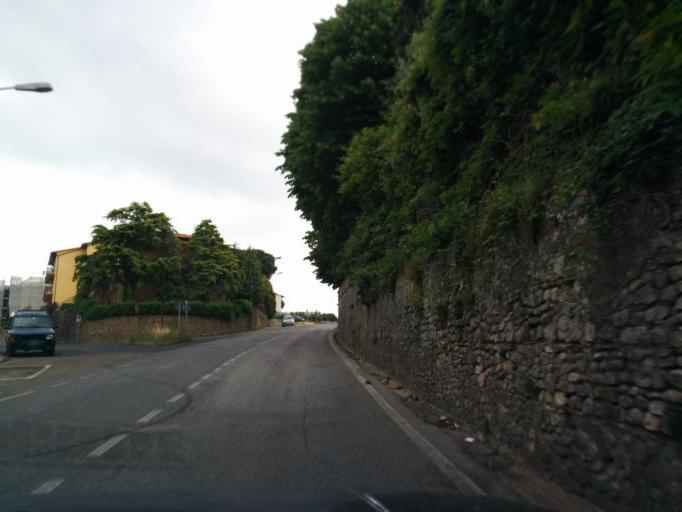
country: IT
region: Tuscany
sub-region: Province of Florence
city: San Casciano in Val di Pesa
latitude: 43.6514
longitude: 11.1820
